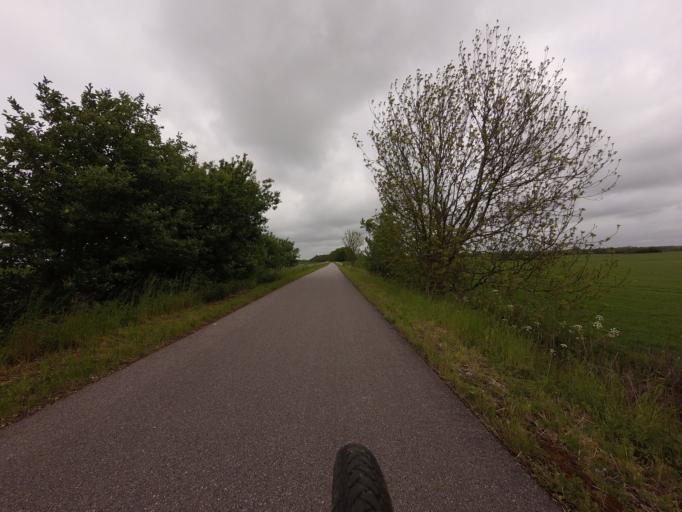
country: DK
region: Zealand
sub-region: Slagelse Kommune
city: Slagelse
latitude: 55.3651
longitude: 11.3855
